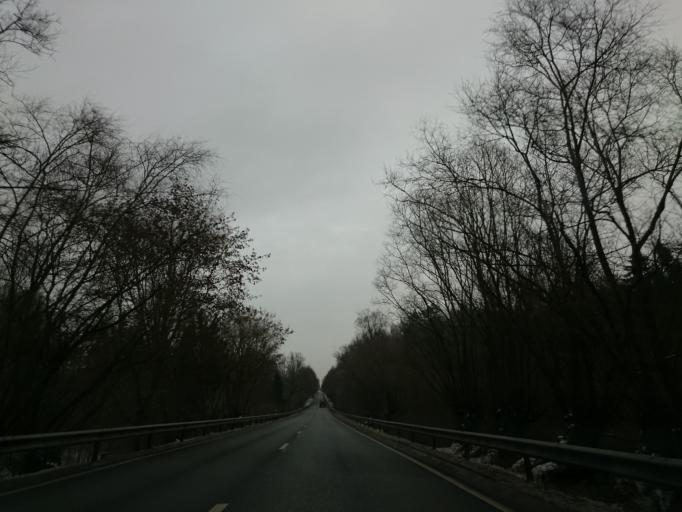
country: LV
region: Seja
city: Loja
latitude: 57.1496
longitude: 24.6816
